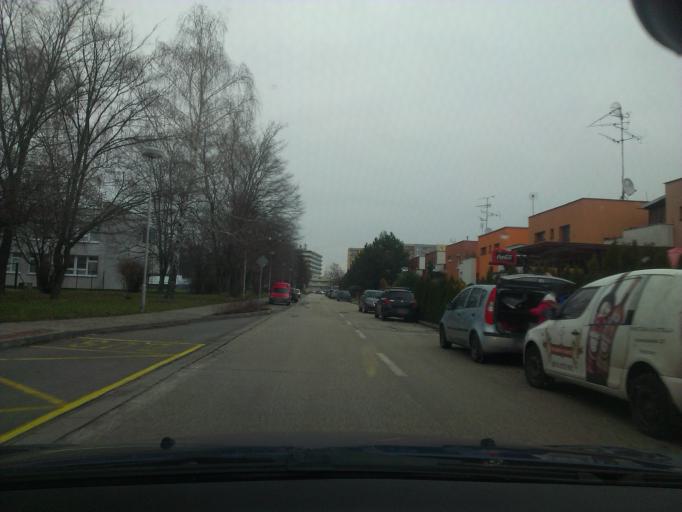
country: SK
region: Trnavsky
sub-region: Okres Trnava
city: Piestany
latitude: 48.5839
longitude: 17.8206
